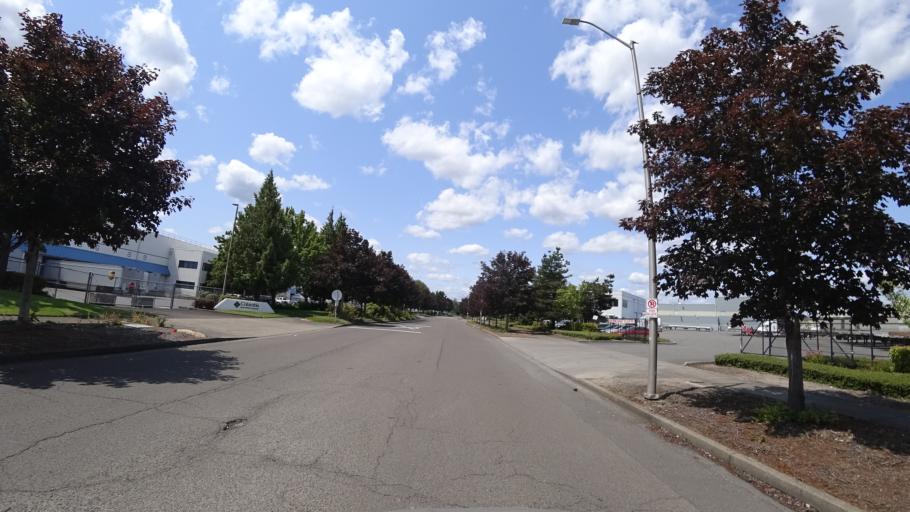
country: US
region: Washington
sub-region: Clark County
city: Lake Shore
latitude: 45.6291
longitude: -122.7473
